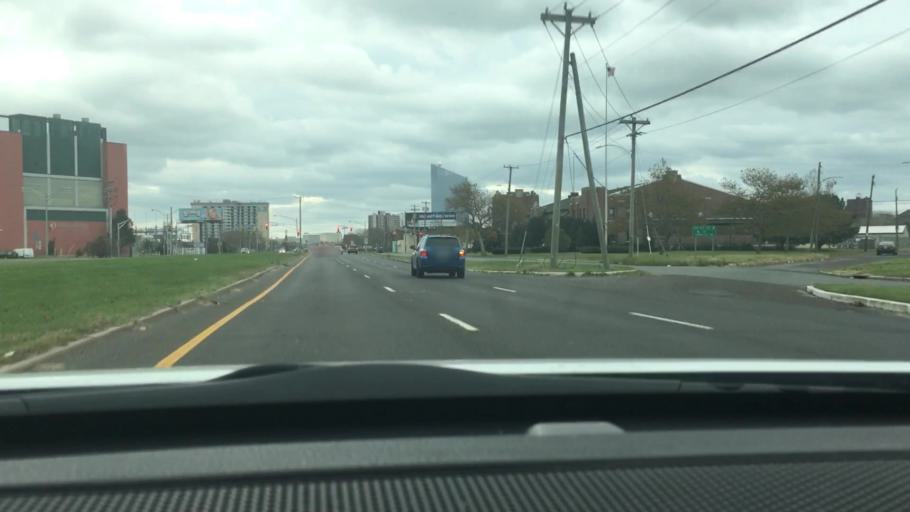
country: US
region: New Jersey
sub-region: Atlantic County
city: Atlantic City
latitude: 39.3732
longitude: -74.4388
